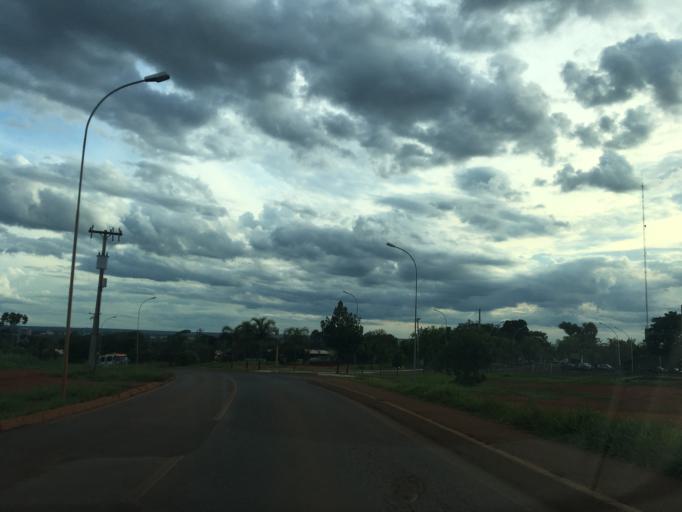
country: BR
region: Federal District
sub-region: Brasilia
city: Brasilia
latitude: -15.8326
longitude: -47.9319
